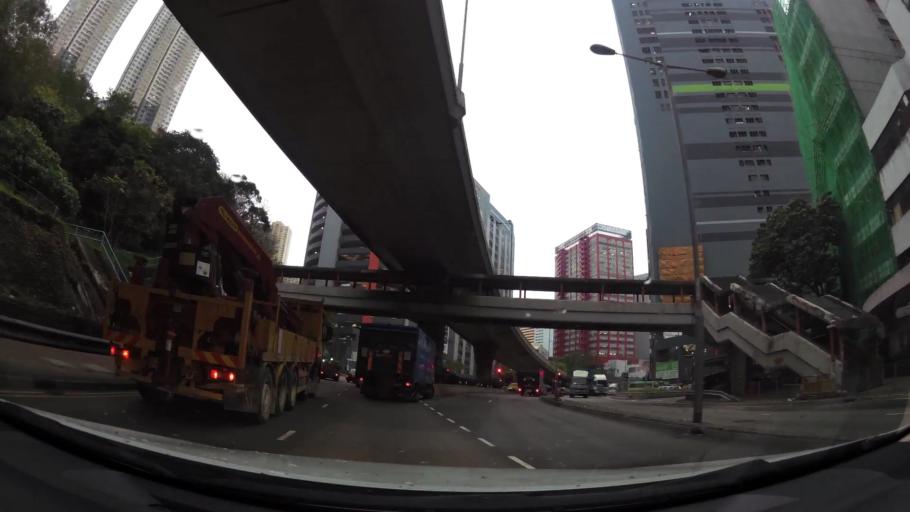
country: HK
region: Tsuen Wan
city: Tsuen Wan
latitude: 22.3661
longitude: 114.1211
